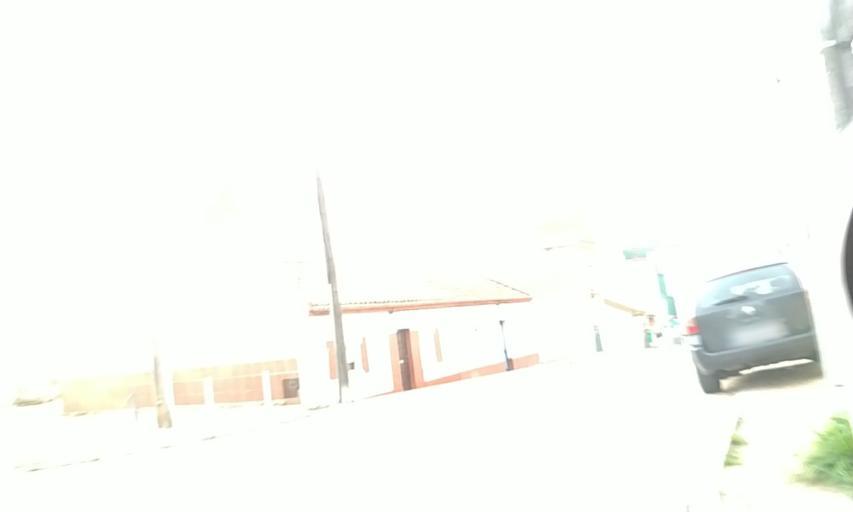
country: PT
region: Setubal
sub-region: Setubal
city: Setubal
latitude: 38.5277
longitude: -8.8672
